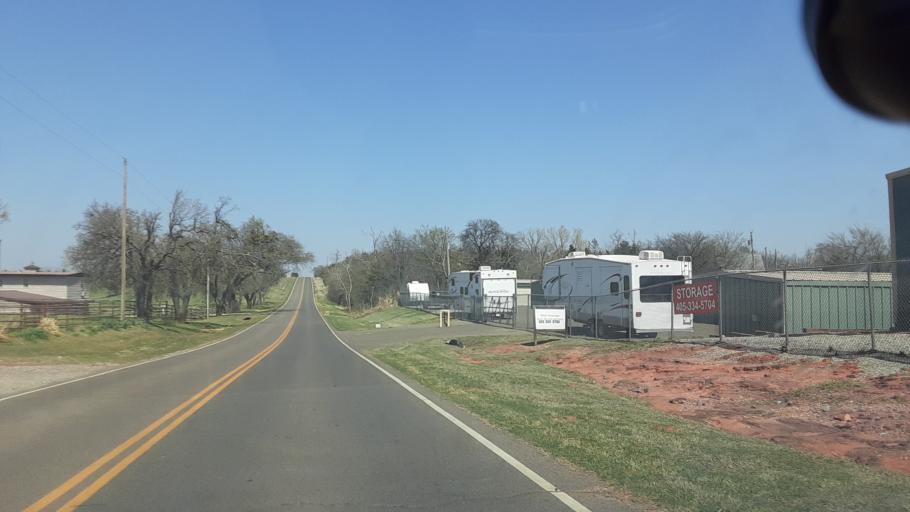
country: US
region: Oklahoma
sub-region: Logan County
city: Guthrie
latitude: 35.7764
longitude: -97.4784
